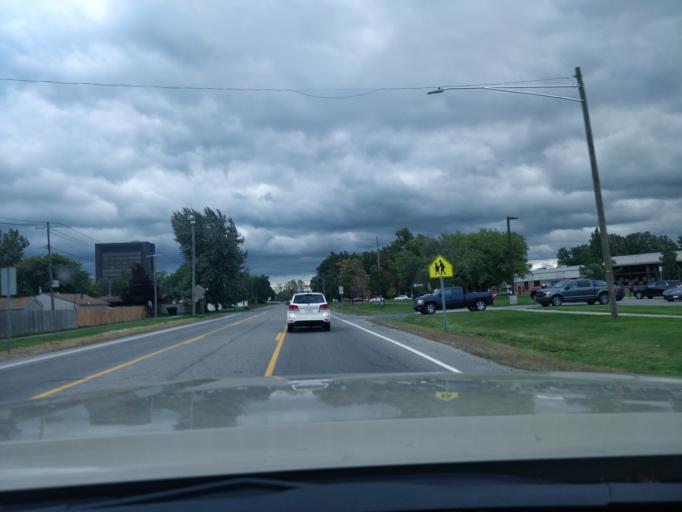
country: US
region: Michigan
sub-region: Wayne County
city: Southgate
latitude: 42.1936
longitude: -83.1934
